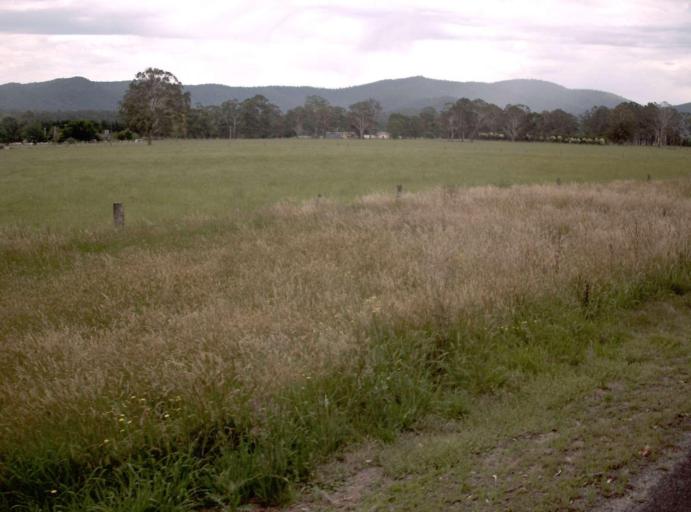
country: AU
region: New South Wales
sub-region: Bombala
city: Bombala
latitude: -37.5255
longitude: 149.1661
